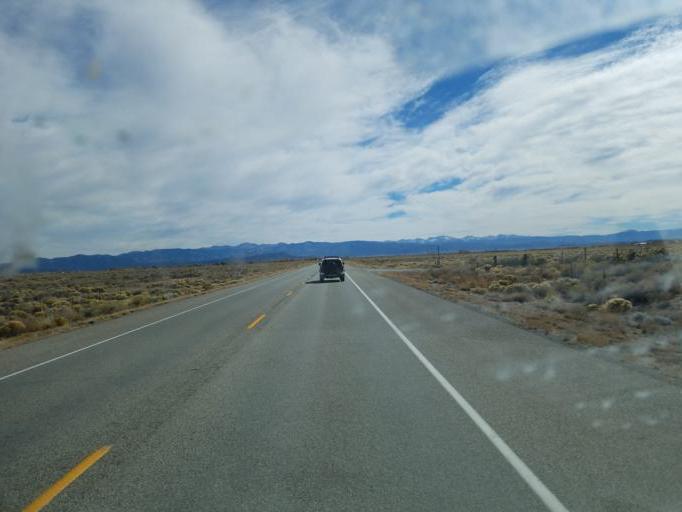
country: US
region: Colorado
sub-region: Costilla County
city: San Luis
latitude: 37.4470
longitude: -105.5376
